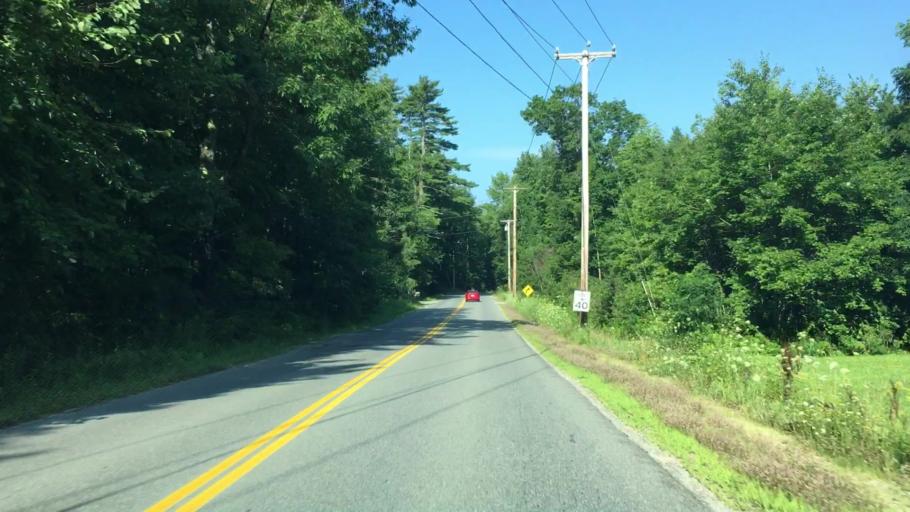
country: US
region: Maine
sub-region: Androscoggin County
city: Minot
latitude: 44.0432
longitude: -70.3204
